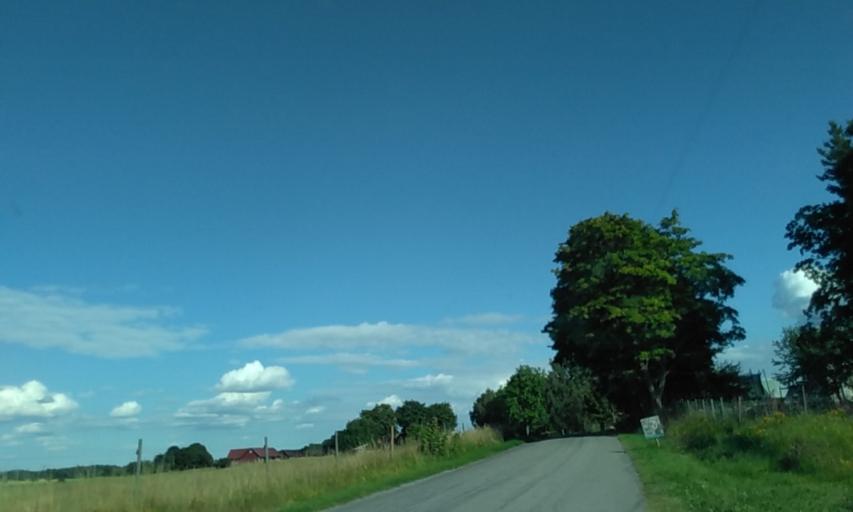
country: SE
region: Vaestra Goetaland
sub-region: Lidkopings Kommun
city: Lidkoping
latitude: 58.5748
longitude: 13.0230
